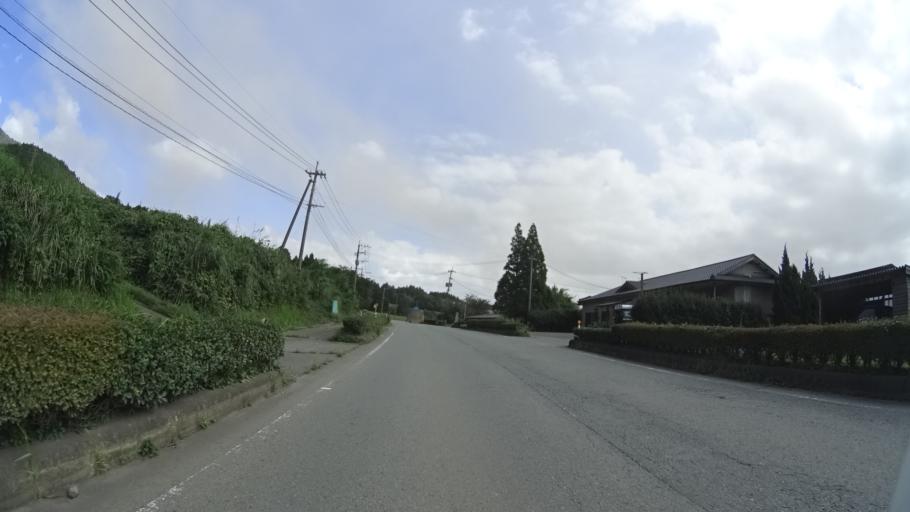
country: JP
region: Kumamoto
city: Aso
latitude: 32.8438
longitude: 131.0430
